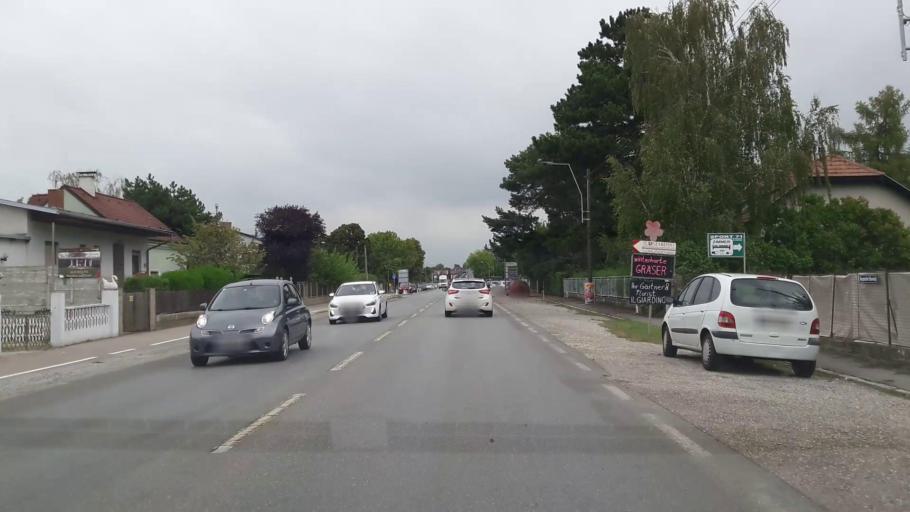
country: AT
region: Lower Austria
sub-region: Politischer Bezirk Ganserndorf
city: Strasshof an der Nordbahn
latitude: 48.3207
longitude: 16.6603
